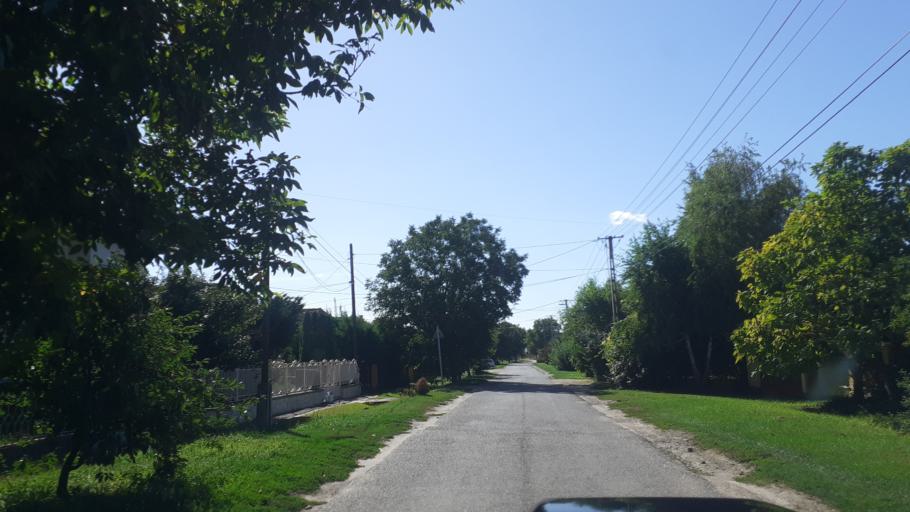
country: HU
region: Fejer
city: Baracska
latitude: 47.2891
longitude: 18.7621
